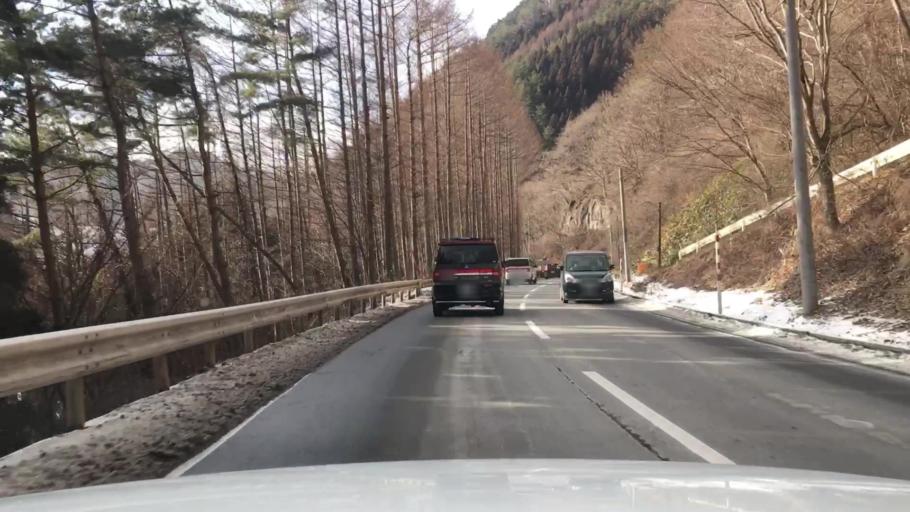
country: JP
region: Iwate
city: Morioka-shi
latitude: 39.6656
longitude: 141.3135
